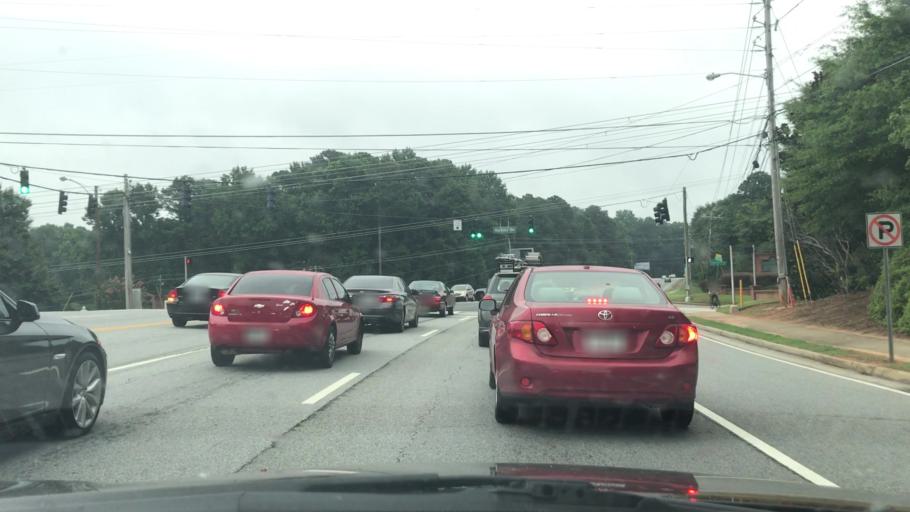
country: US
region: Georgia
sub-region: Gwinnett County
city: Lilburn
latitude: 33.8890
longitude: -84.1554
